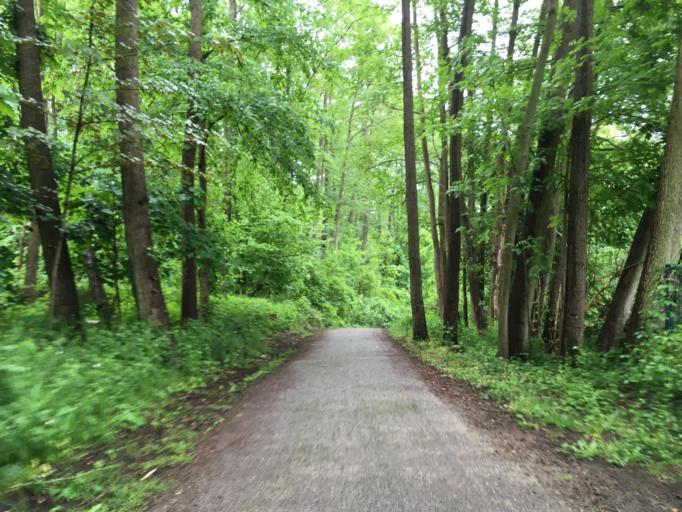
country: DE
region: Brandenburg
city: Eberswalde
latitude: 52.8429
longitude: 13.7574
